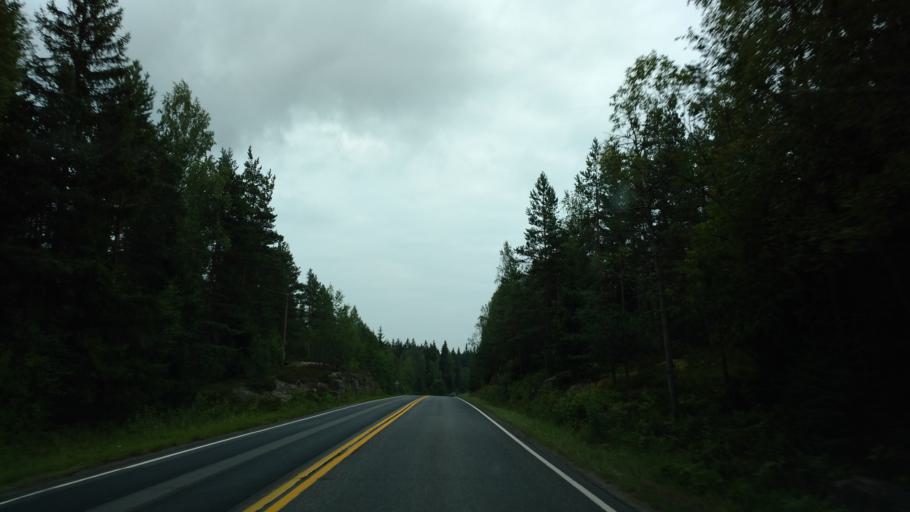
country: FI
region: Varsinais-Suomi
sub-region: Salo
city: Halikko
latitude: 60.4515
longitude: 23.0291
